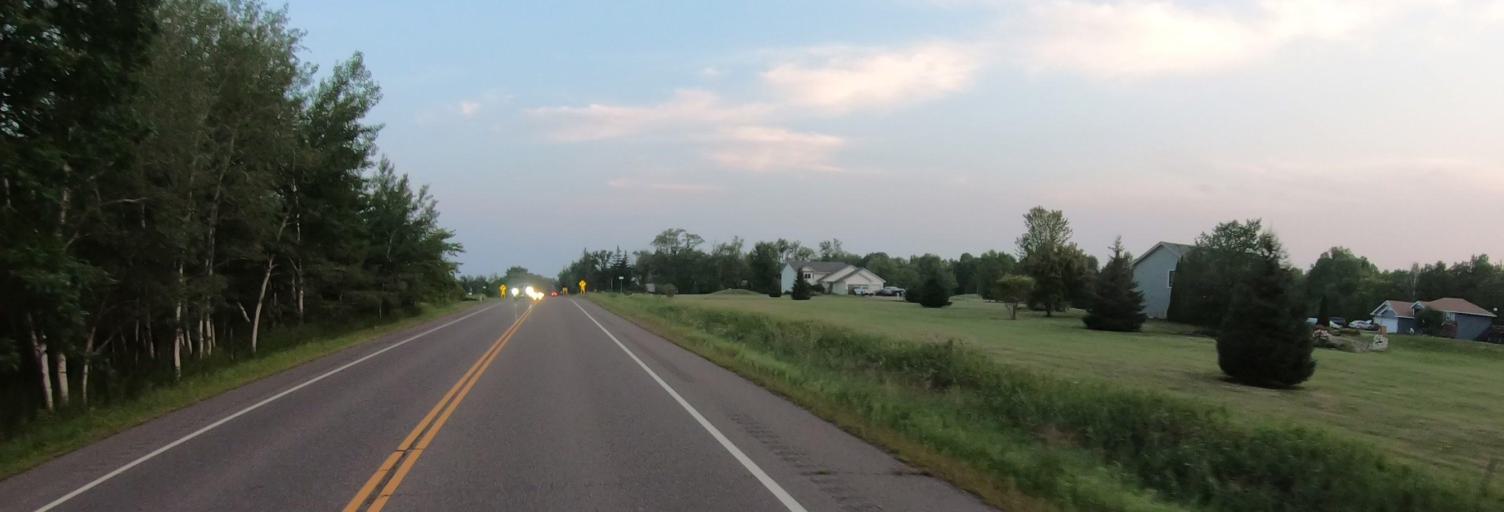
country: US
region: Minnesota
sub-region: Pine County
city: Rock Creek
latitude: 45.7692
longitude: -92.9602
